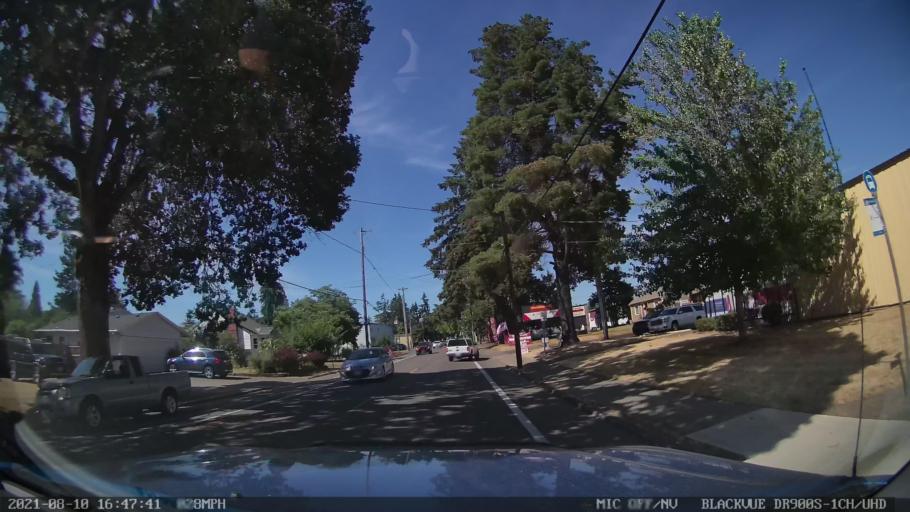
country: US
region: Oregon
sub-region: Marion County
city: Salem
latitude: 44.9633
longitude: -123.0193
